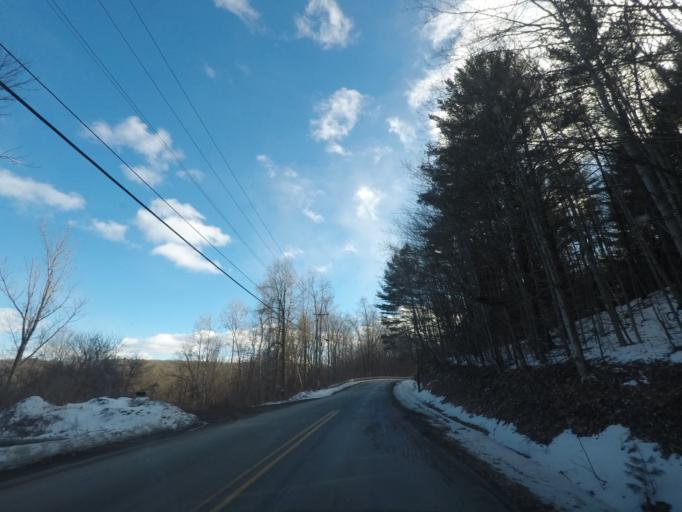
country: US
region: New York
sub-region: Rensselaer County
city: Hoosick Falls
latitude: 42.8230
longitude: -73.3893
